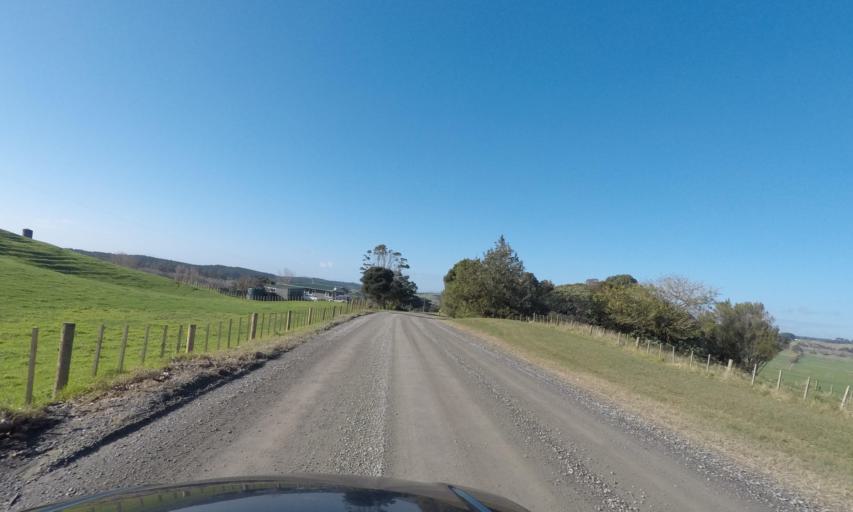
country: NZ
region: Auckland
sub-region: Auckland
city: Wellsford
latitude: -36.1430
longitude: 174.5955
